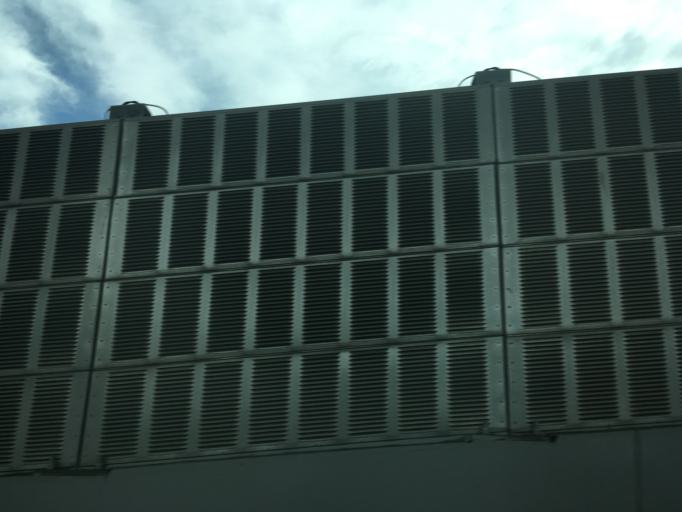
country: JP
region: Hyogo
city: Ashiya
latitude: 34.7116
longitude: 135.3016
